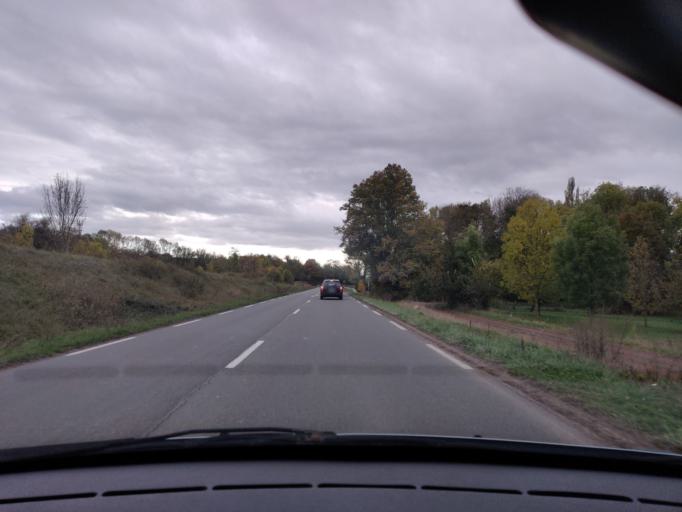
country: FR
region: Auvergne
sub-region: Departement du Puy-de-Dome
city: Saint-Bonnet-pres-Riom
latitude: 45.9189
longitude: 3.1222
